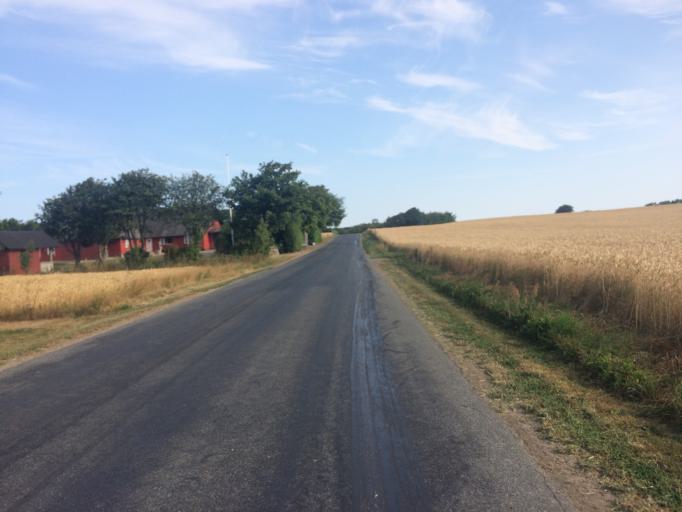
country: DK
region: Central Jutland
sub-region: Holstebro Kommune
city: Vinderup
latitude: 56.5841
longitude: 8.7567
